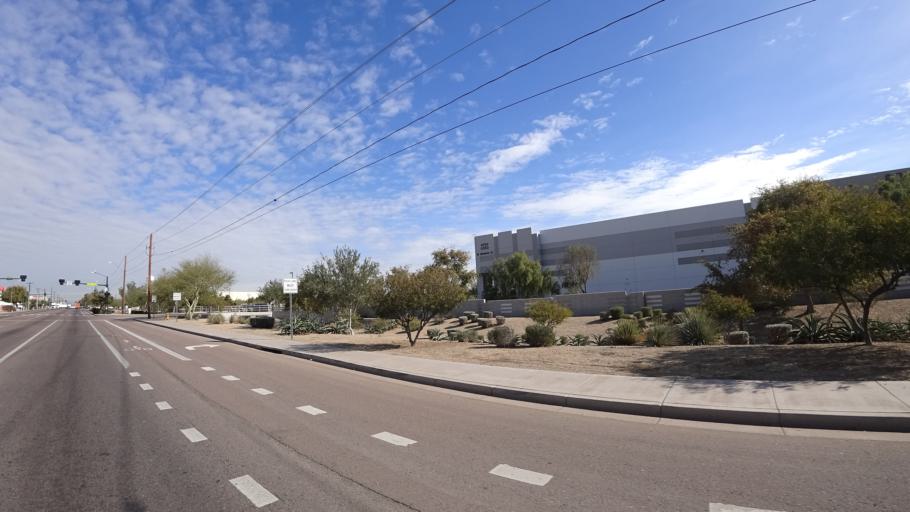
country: US
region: Arizona
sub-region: Maricopa County
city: Laveen
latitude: 33.4327
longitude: -112.1692
